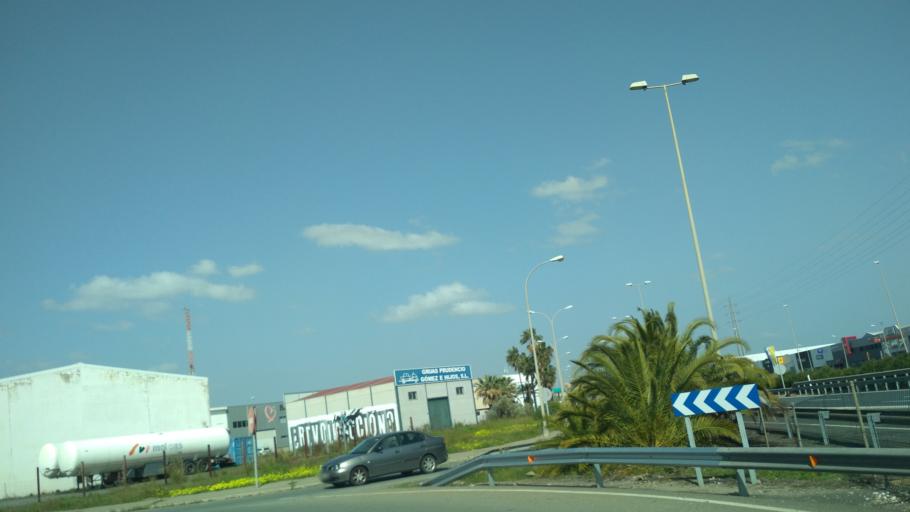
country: ES
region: Andalusia
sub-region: Provincia de Huelva
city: Huelva
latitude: 37.2607
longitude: -6.9204
